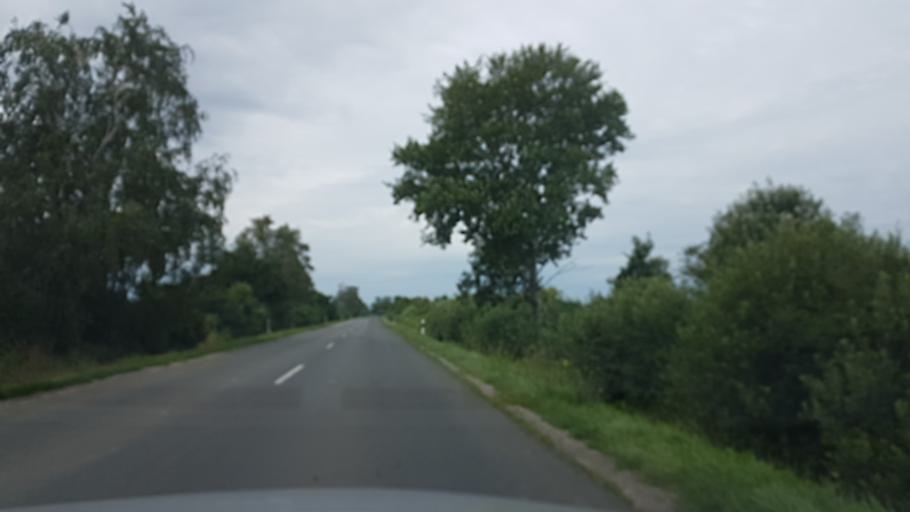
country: HU
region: Baranya
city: Szigetvar
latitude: 46.0449
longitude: 17.7616
